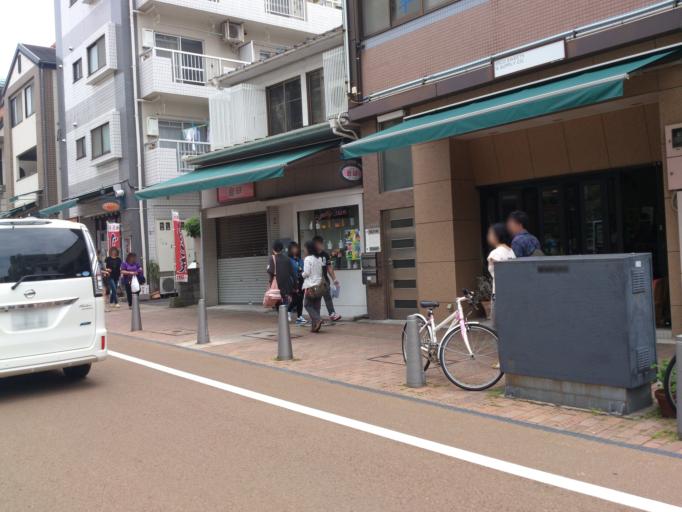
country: JP
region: Ehime
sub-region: Shikoku-chuo Shi
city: Matsuyama
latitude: 33.8436
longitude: 132.7713
